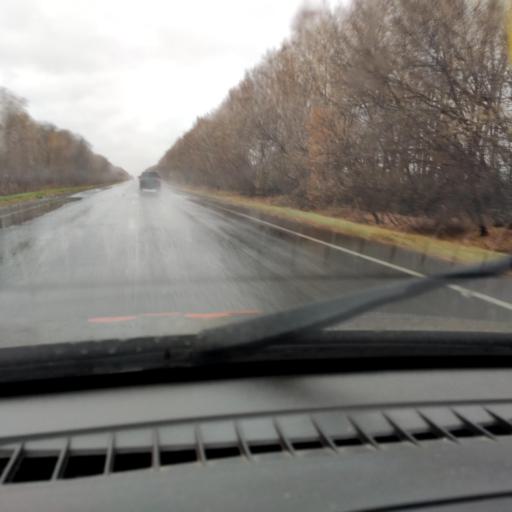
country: RU
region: Samara
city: Tol'yatti
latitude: 53.6017
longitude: 49.3220
